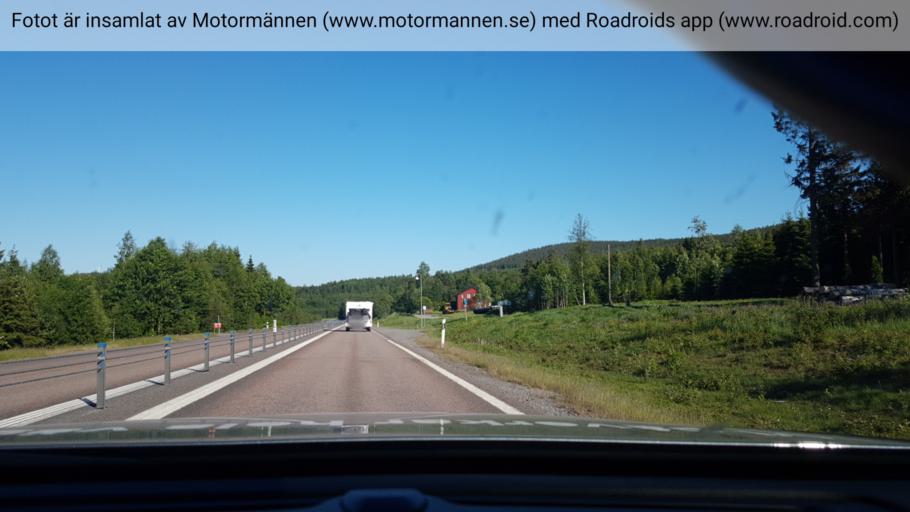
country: SE
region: Vaesternorrland
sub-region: Haernoesands Kommun
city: Haernoesand
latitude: 62.6118
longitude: 17.8615
